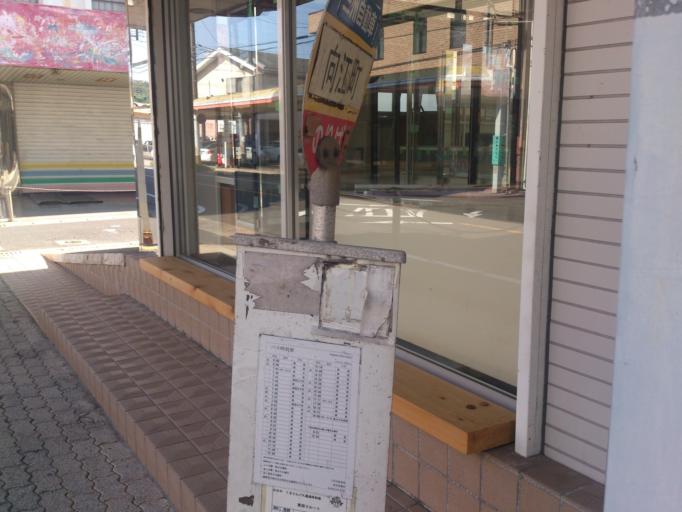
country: JP
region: Kagoshima
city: Kanoya
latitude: 31.3852
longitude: 130.8511
